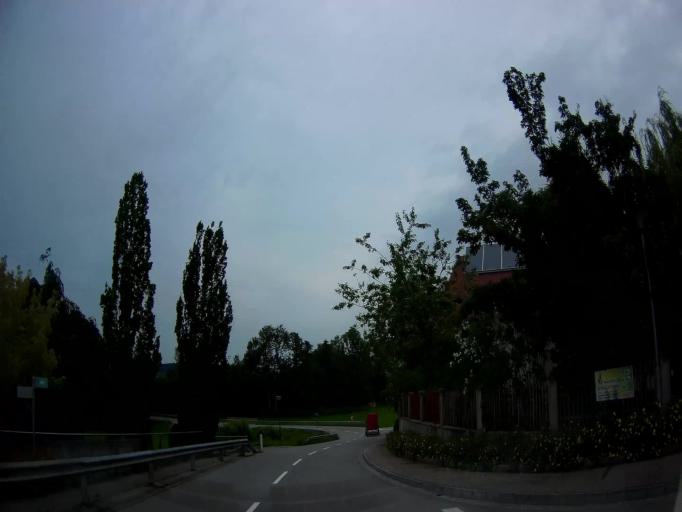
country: AT
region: Salzburg
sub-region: Politischer Bezirk Salzburg-Umgebung
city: Mattsee
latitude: 48.0466
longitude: 13.1502
